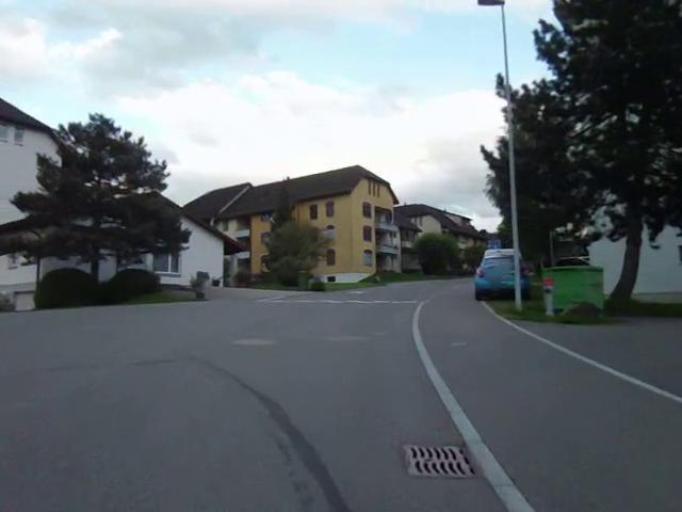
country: CH
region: Zurich
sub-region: Bezirk Hinwil
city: Rueti / Dorfzentrum, Suedl. Teil
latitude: 47.2510
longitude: 8.8580
